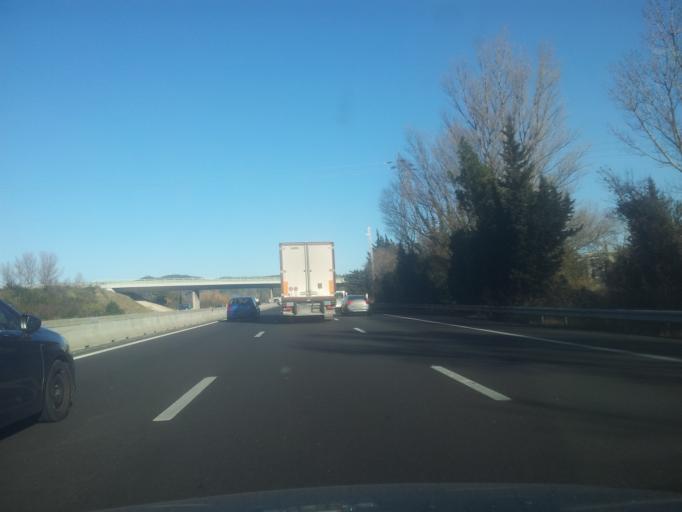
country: FR
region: Provence-Alpes-Cote d'Azur
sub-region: Departement du Vaucluse
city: Bollene
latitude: 44.2837
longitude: 4.7370
